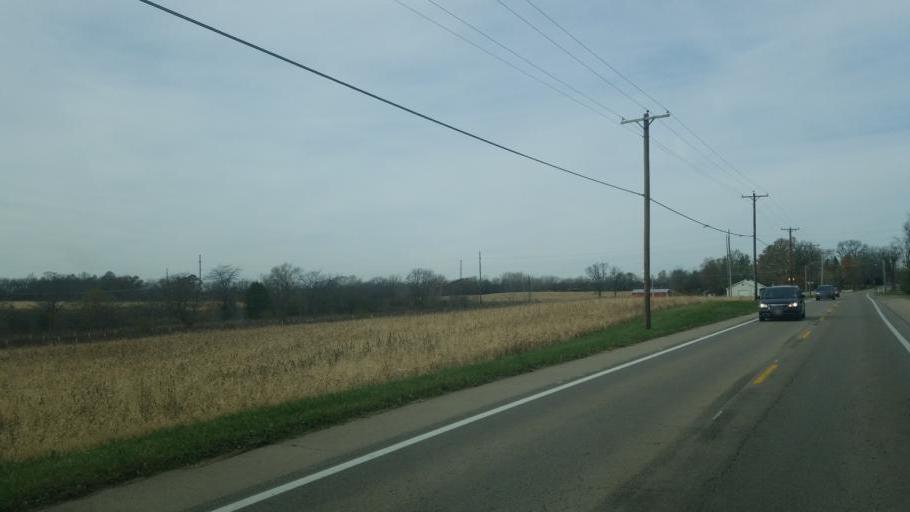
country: US
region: Ohio
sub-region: Madison County
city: London
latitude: 39.8959
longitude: -83.4602
